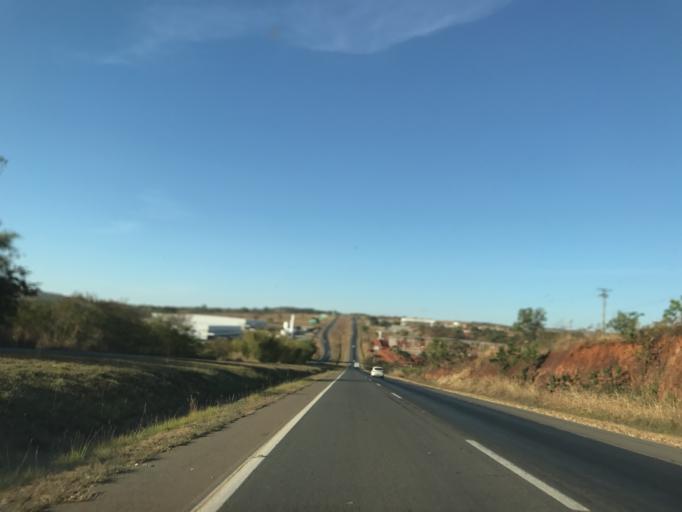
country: BR
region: Goias
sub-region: Aparecida De Goiania
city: Aparecida de Goiania
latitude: -16.8668
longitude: -49.2504
